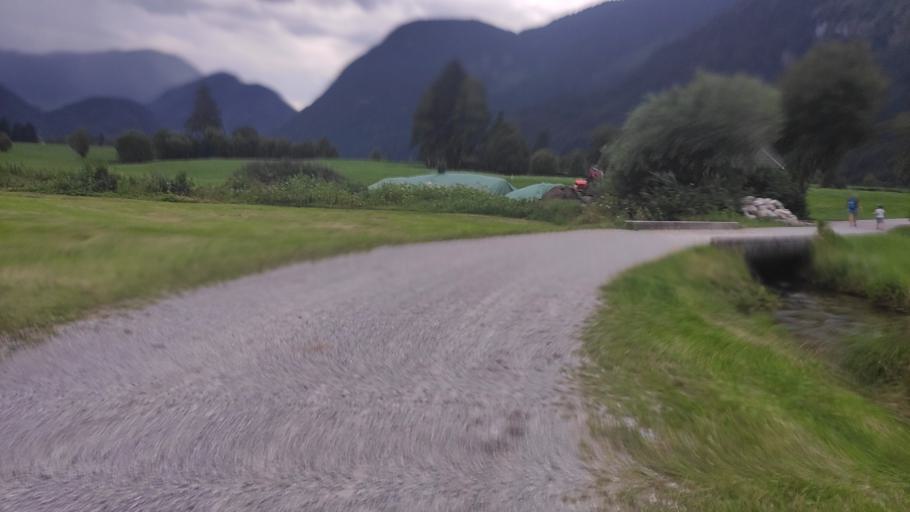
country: AT
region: Salzburg
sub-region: Politischer Bezirk Zell am See
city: Lofer
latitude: 47.5799
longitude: 12.6923
